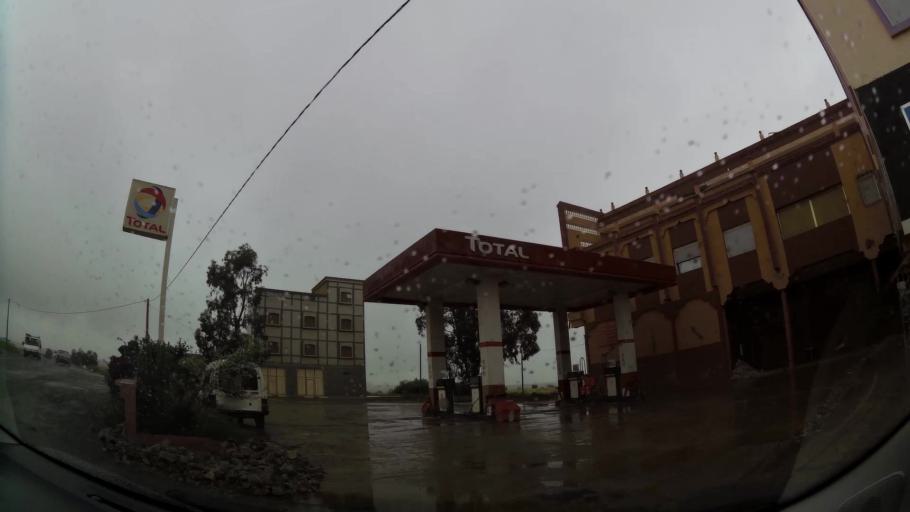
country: MA
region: Oriental
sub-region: Nador
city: Boudinar
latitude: 35.1297
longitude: -3.6287
